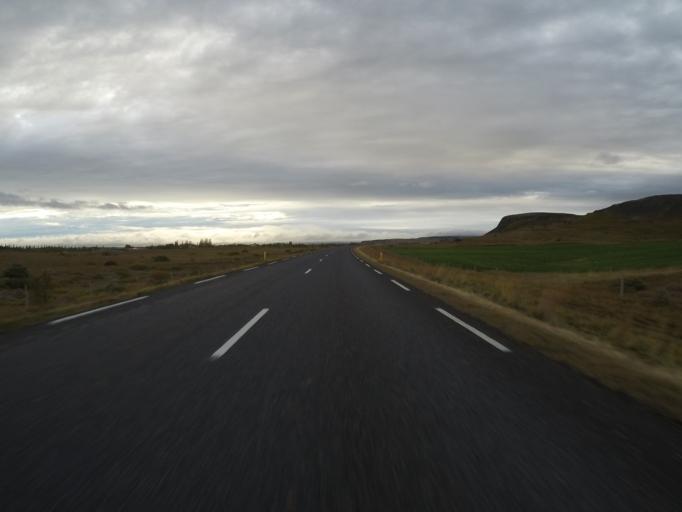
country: IS
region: South
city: Vestmannaeyjar
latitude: 64.0413
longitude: -20.2019
